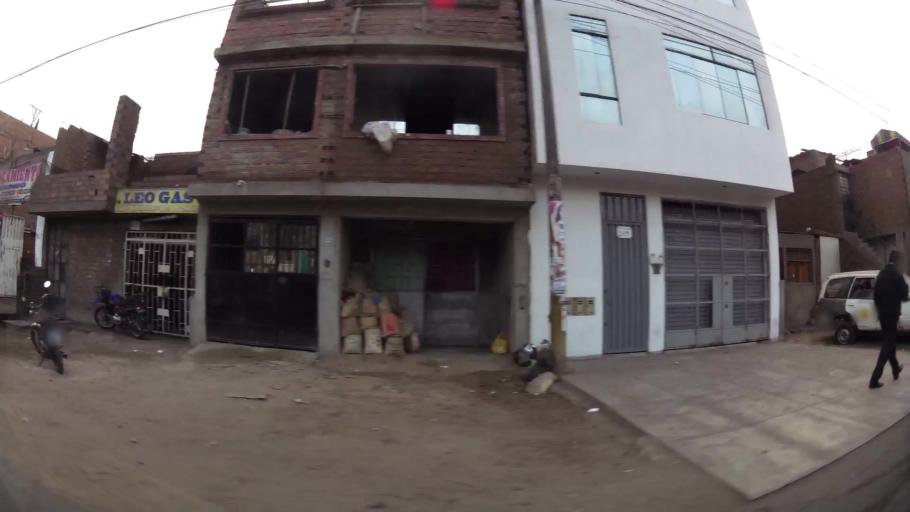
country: PE
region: Lima
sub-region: Lima
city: Independencia
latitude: -11.9869
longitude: -77.0037
